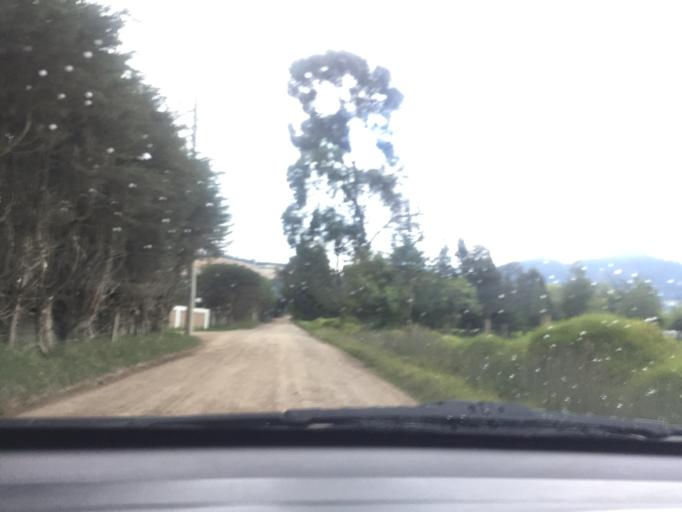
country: CO
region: Cundinamarca
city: Cogua
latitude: 5.0683
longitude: -73.9332
